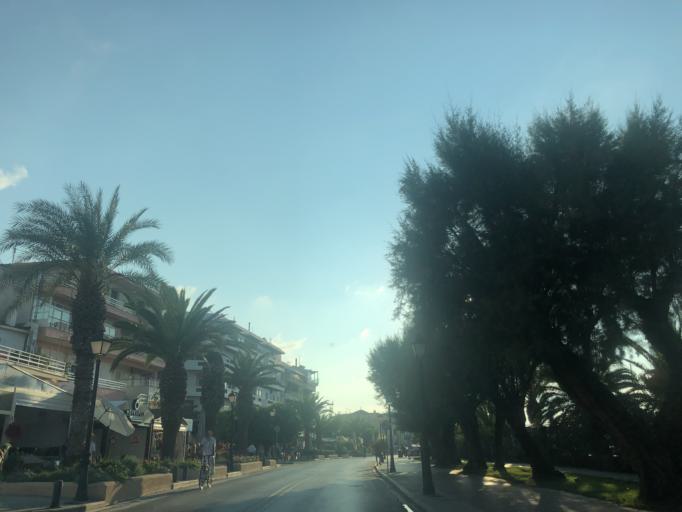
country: GR
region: Crete
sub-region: Nomos Rethymnis
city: Rethymno
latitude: 35.3667
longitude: 24.4819
